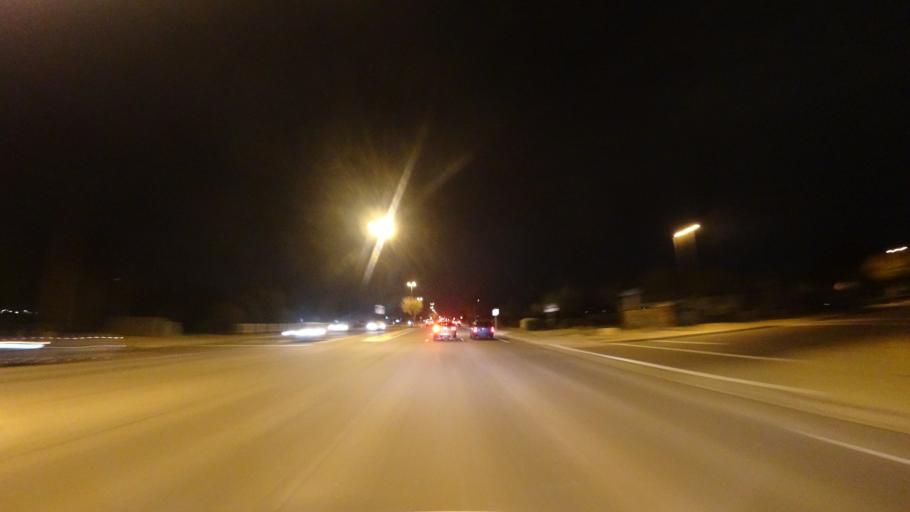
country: US
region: Arizona
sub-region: Maricopa County
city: Gilbert
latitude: 33.3311
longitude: -111.7558
